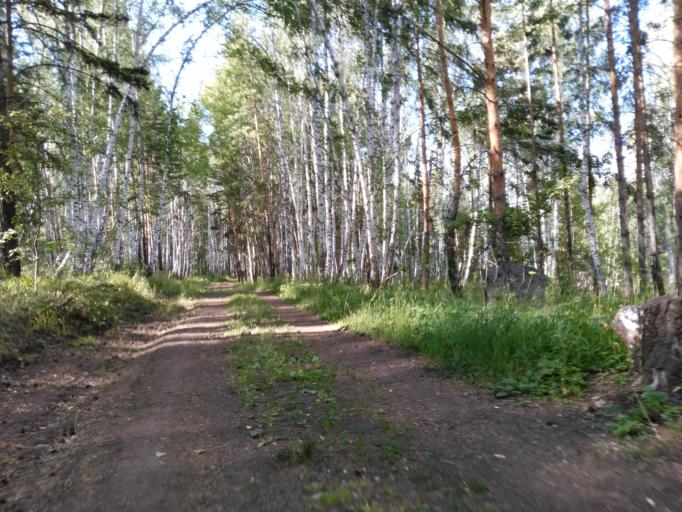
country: RU
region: Bashkortostan
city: Uchaly
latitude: 54.3308
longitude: 59.3580
